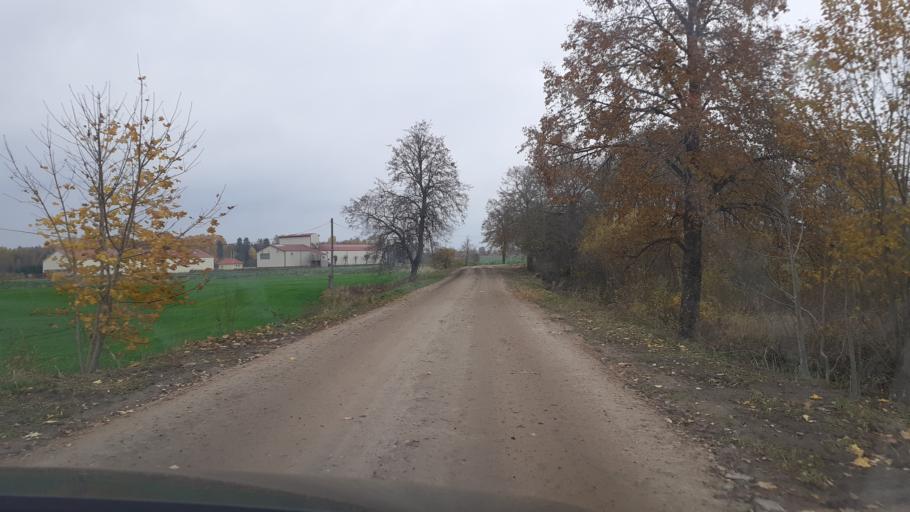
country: LV
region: Skrunda
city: Skrunda
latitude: 56.8514
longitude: 22.2143
